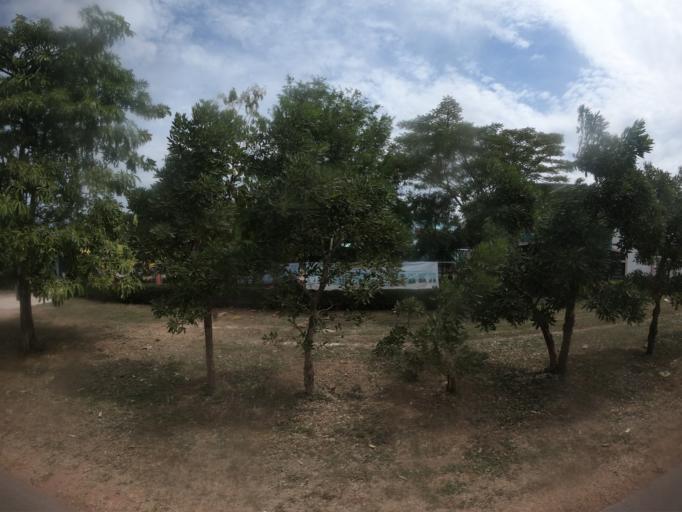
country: TH
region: Maha Sarakham
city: Chiang Yuen
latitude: 16.3856
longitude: 103.1025
